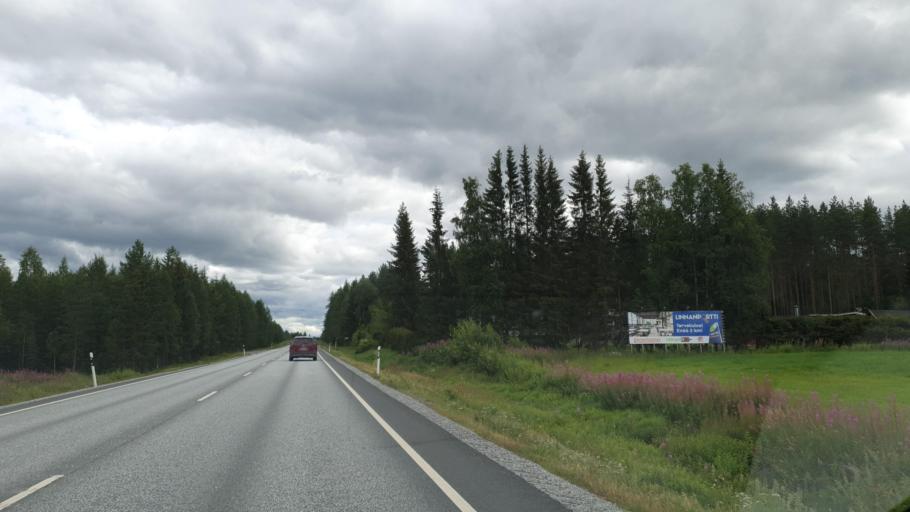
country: FI
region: Northern Savo
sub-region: Ylae-Savo
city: Sonkajaervi
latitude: 63.8913
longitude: 27.4224
